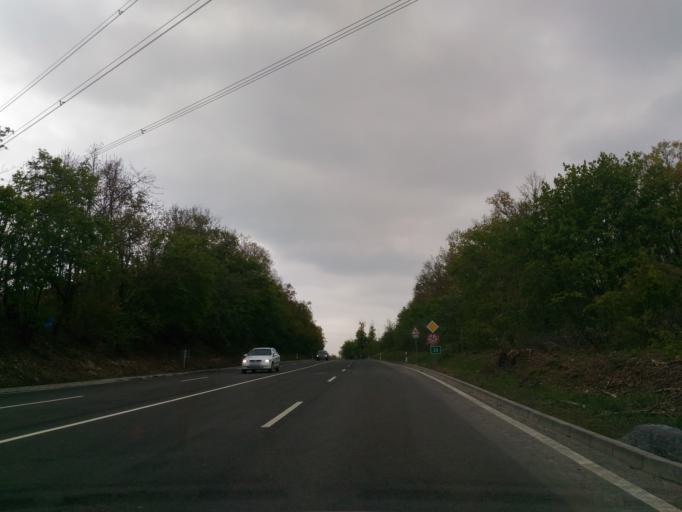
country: HU
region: Pest
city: Kerepes
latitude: 47.5804
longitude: 19.2921
